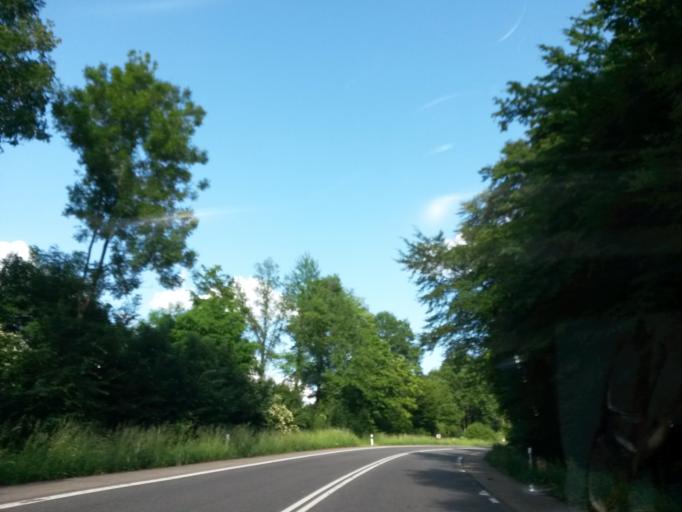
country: DE
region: North Rhine-Westphalia
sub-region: Regierungsbezirk Koln
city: Much
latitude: 50.9212
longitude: 7.3701
